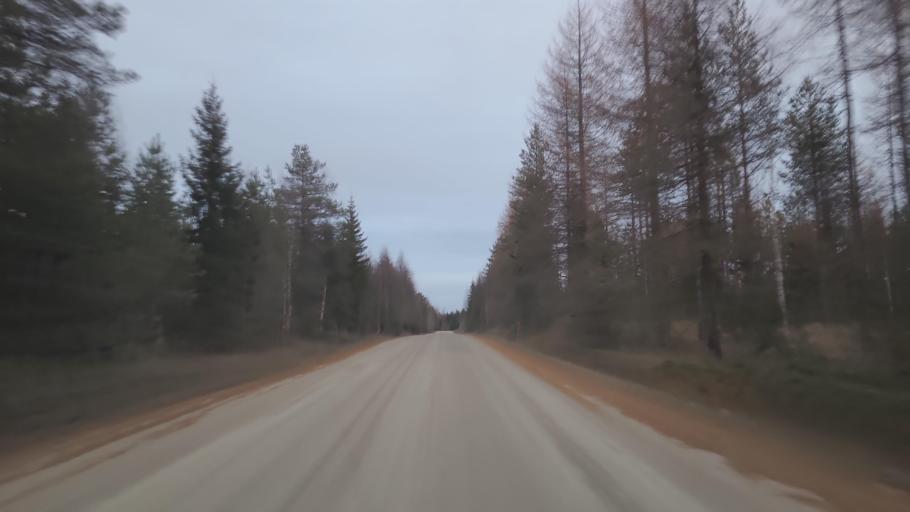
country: FI
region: Lapland
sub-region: Kemi-Tornio
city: Tervola
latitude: 66.0714
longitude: 24.8774
